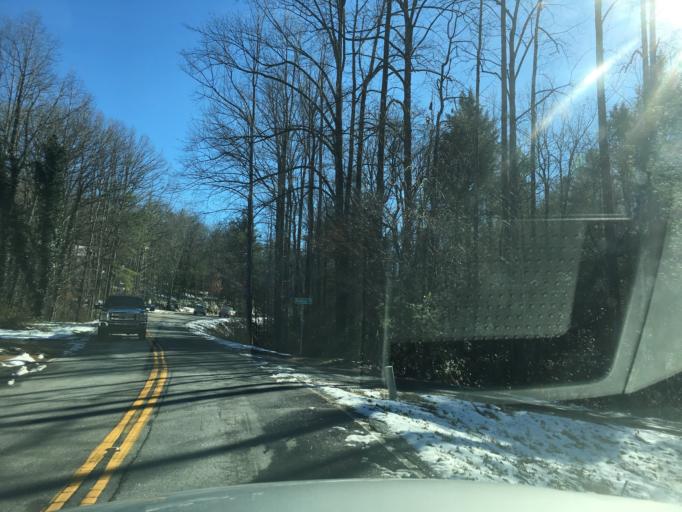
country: US
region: South Carolina
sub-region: Greenville County
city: Slater-Marietta
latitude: 35.0648
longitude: -82.6186
